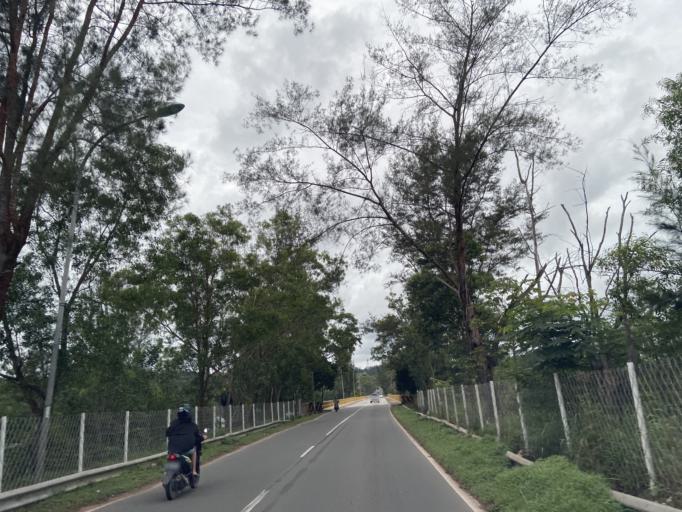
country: SG
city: Singapore
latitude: 1.1116
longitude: 104.0114
